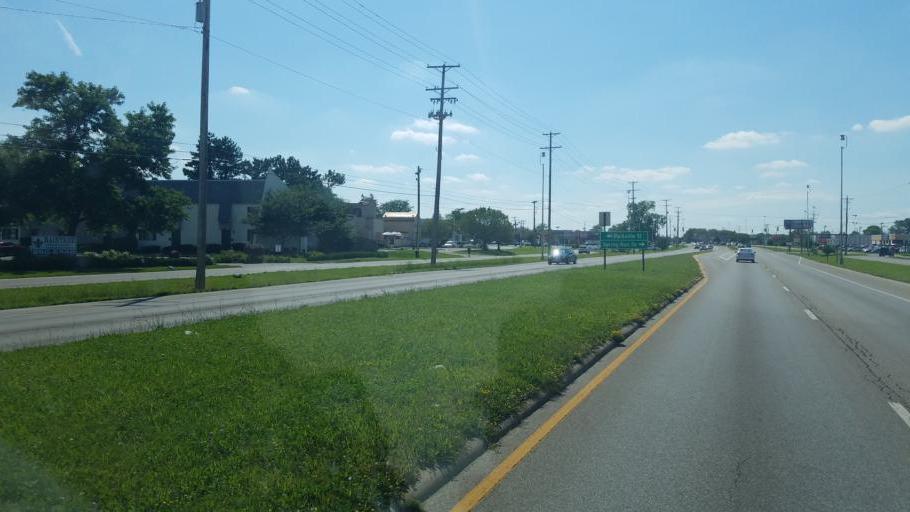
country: US
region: Ohio
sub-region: Franklin County
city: Minerva Park
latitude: 40.0857
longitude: -82.9541
